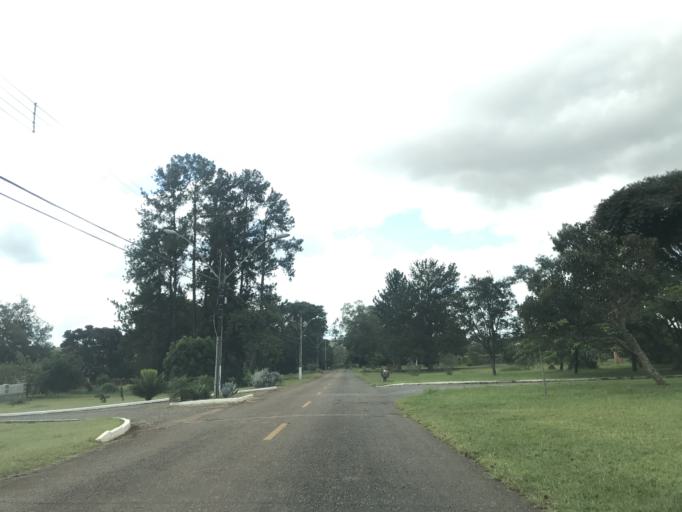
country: BR
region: Federal District
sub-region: Brasilia
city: Brasilia
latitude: -15.8894
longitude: -47.9246
